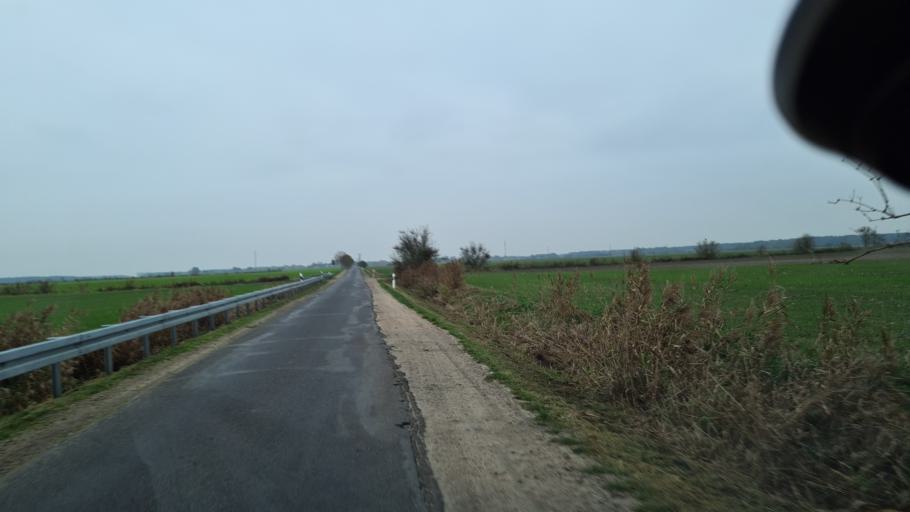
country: DE
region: Brandenburg
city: Ruthnick
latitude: 52.9200
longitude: 12.9926
